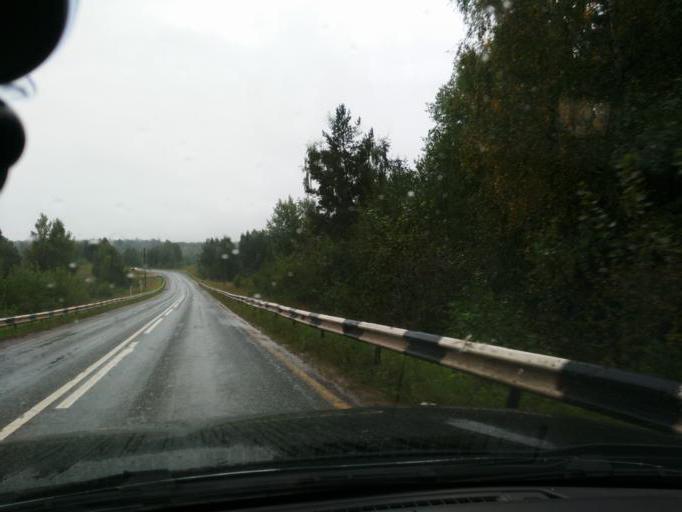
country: RU
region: Perm
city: Yugo-Kamskiy
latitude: 57.5698
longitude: 55.6818
